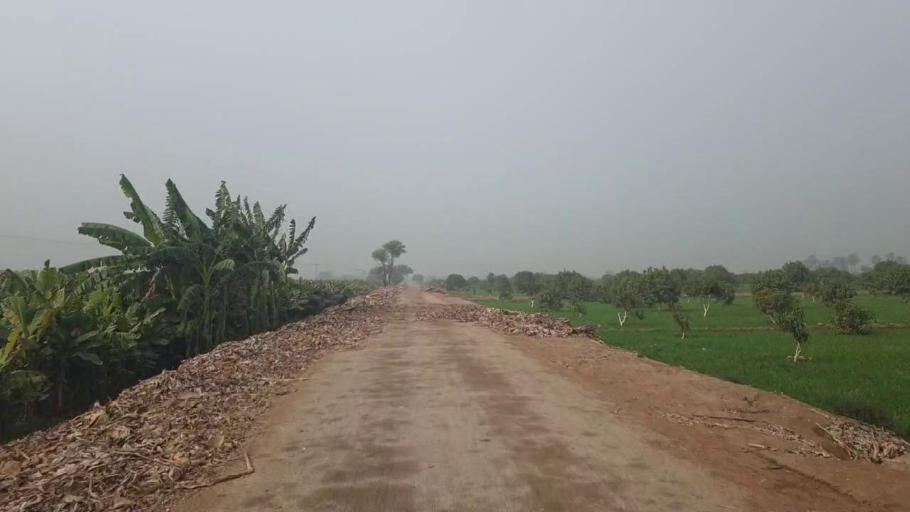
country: PK
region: Sindh
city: Tando Adam
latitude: 25.7215
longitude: 68.6342
